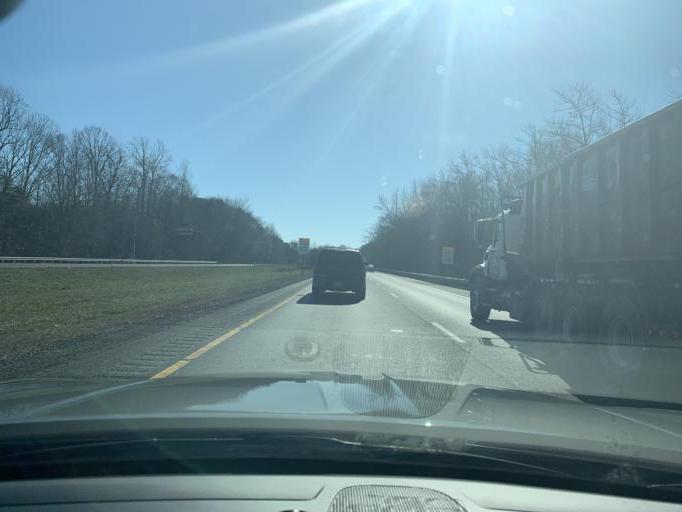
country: US
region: Maryland
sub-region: Prince George's County
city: Clinton
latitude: 38.7467
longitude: -76.8796
